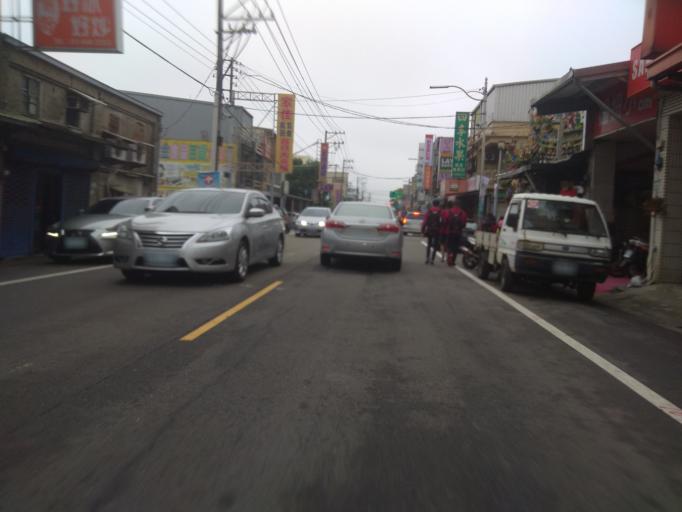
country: TW
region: Taiwan
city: Taoyuan City
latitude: 25.0135
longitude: 121.1348
